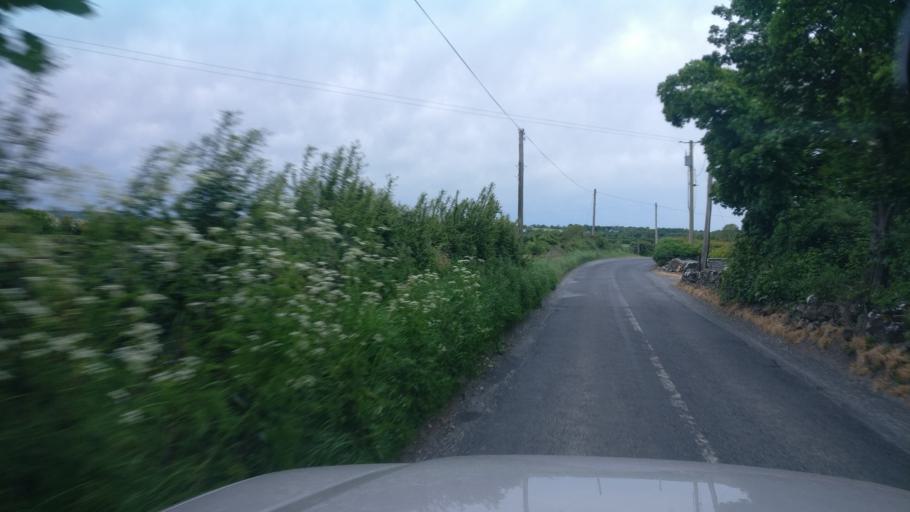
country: IE
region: Connaught
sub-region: County Galway
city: Portumna
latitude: 53.1136
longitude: -8.2952
